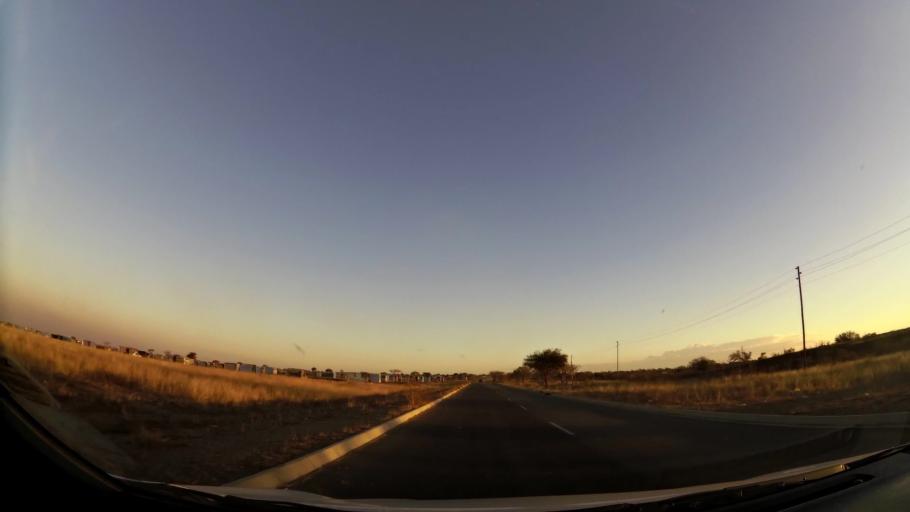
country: ZA
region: Limpopo
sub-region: Capricorn District Municipality
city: Polokwane
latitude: -23.8627
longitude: 29.3736
